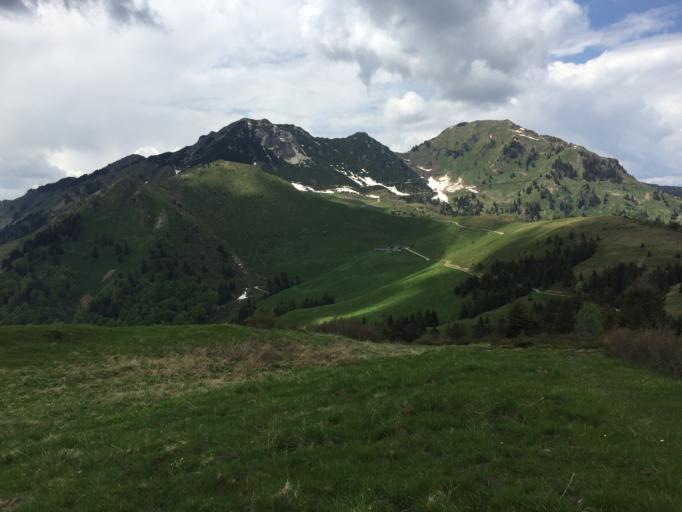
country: IT
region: Friuli Venezia Giulia
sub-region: Provincia di Udine
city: Sutrio
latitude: 46.4784
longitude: 12.9639
